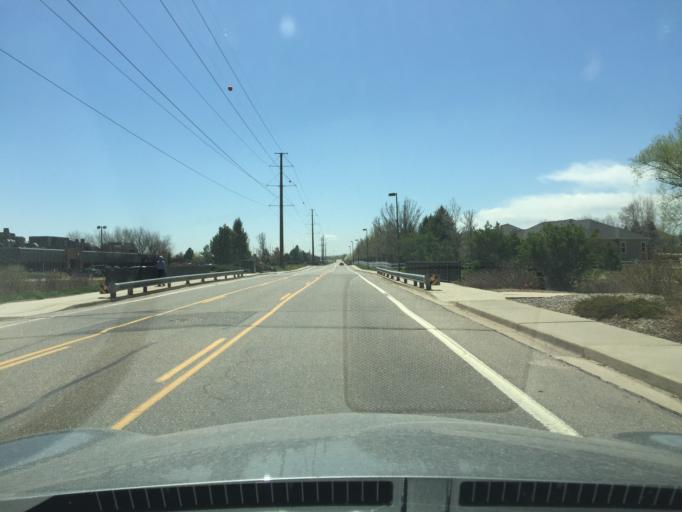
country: US
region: Colorado
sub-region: Boulder County
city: Longmont
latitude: 40.1489
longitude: -105.1404
